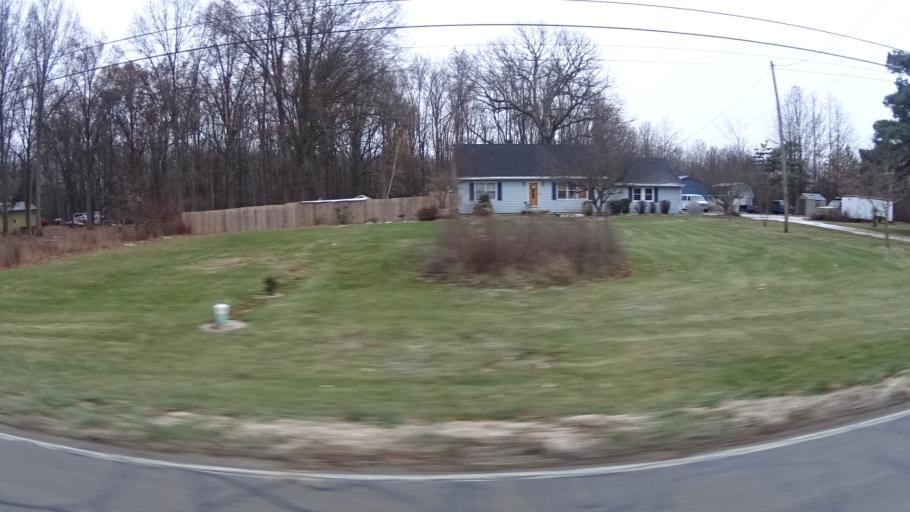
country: US
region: Ohio
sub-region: Lorain County
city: Eaton Estates
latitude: 41.2974
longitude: -82.0337
